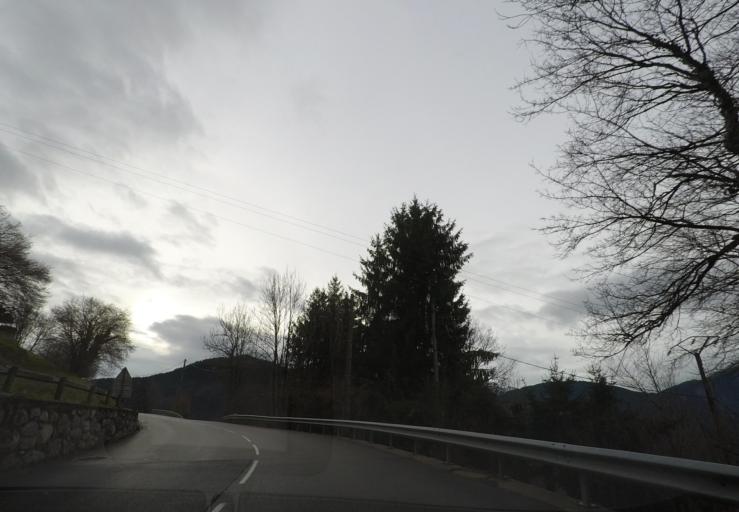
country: FR
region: Rhone-Alpes
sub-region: Departement de la Haute-Savoie
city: Chatillon-sur-Cluses
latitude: 46.0791
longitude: 6.5934
